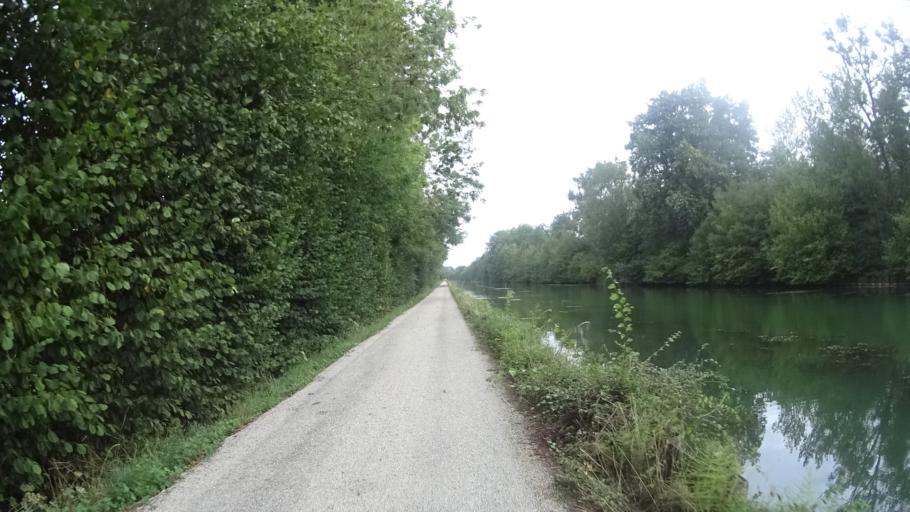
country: FR
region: Picardie
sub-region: Departement de l'Aisne
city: Ribemont
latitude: 49.7812
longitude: 3.4087
